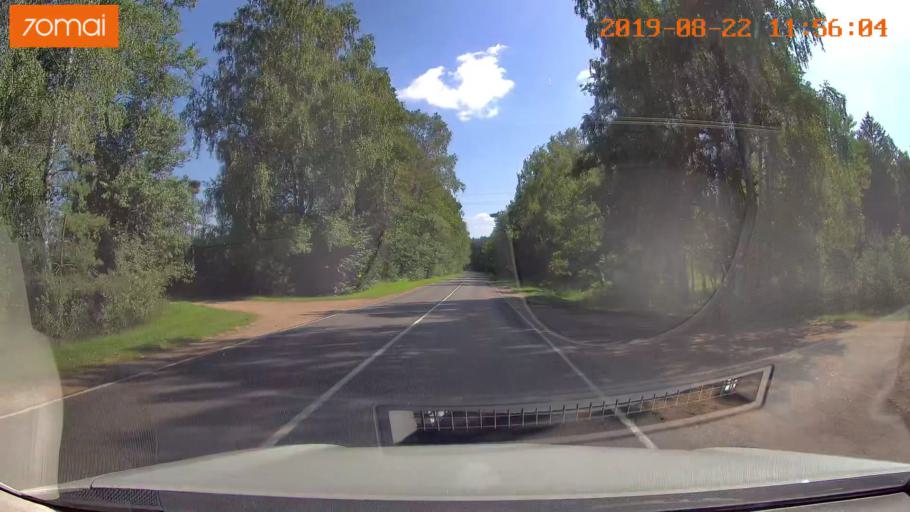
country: BY
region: Minsk
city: Prawdzinski
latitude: 53.4294
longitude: 27.5625
